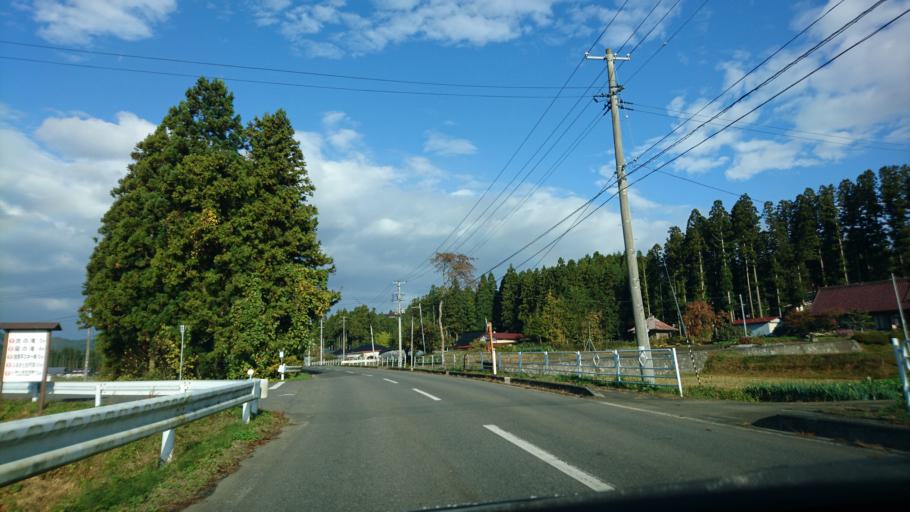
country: JP
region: Iwate
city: Mizusawa
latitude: 39.0441
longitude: 141.0600
